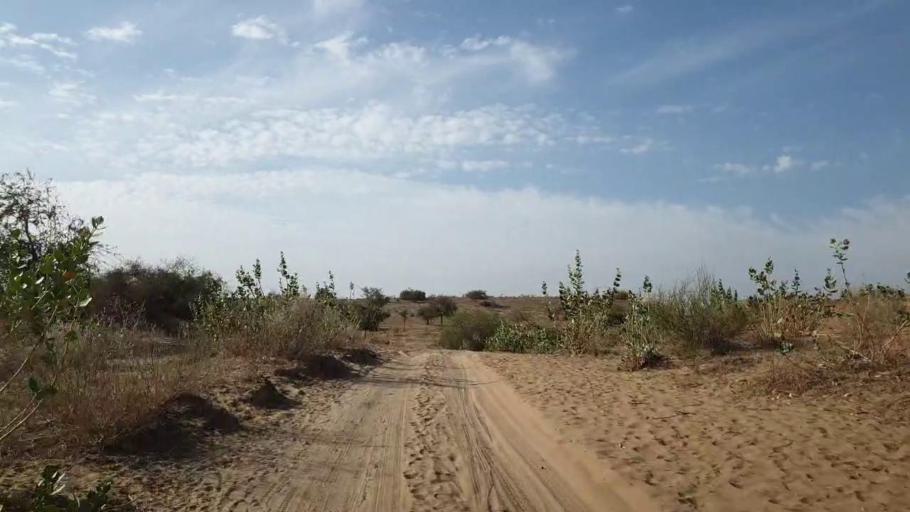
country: PK
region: Sindh
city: Nabisar
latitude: 25.0417
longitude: 69.9756
